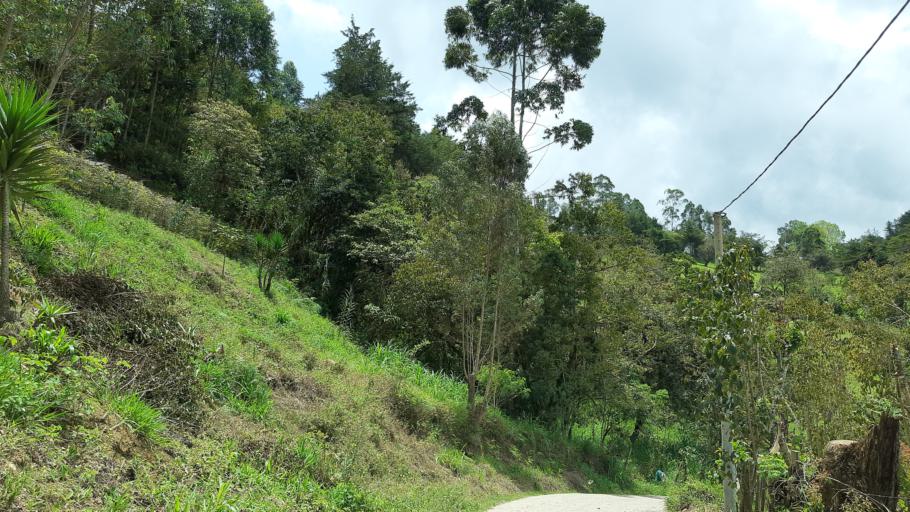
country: CO
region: Boyaca
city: Garagoa
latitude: 5.0725
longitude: -73.3619
